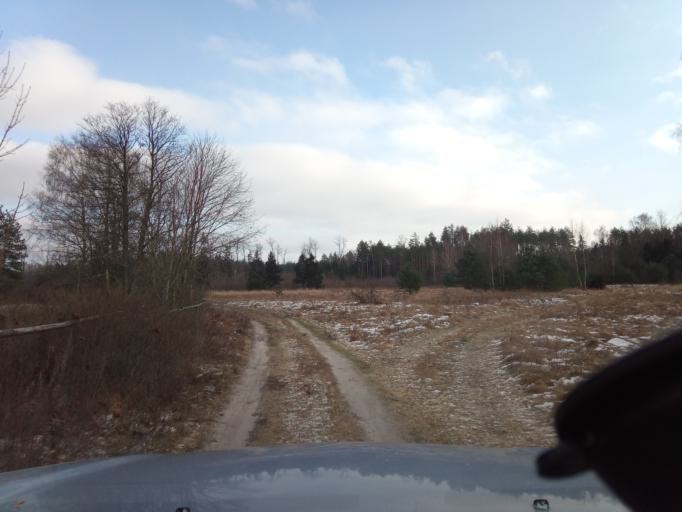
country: LT
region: Alytaus apskritis
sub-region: Alytaus rajonas
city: Daugai
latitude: 54.1108
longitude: 24.2315
